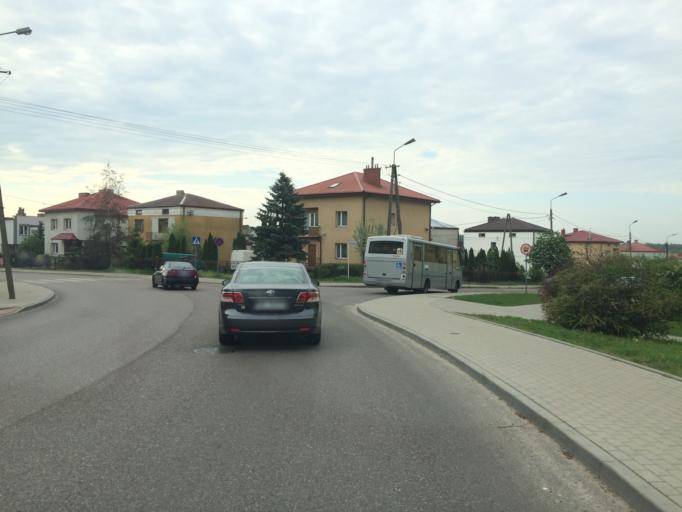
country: PL
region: Masovian Voivodeship
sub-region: Powiat mlawski
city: Mlawa
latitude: 53.1082
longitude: 20.3733
